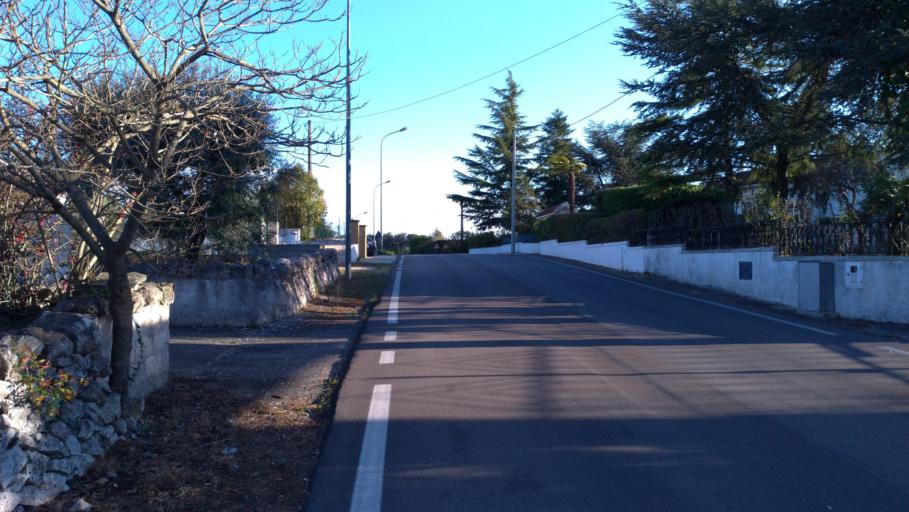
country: IT
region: Apulia
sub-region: Provincia di Taranto
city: Martina Franca
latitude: 40.6883
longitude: 17.3346
